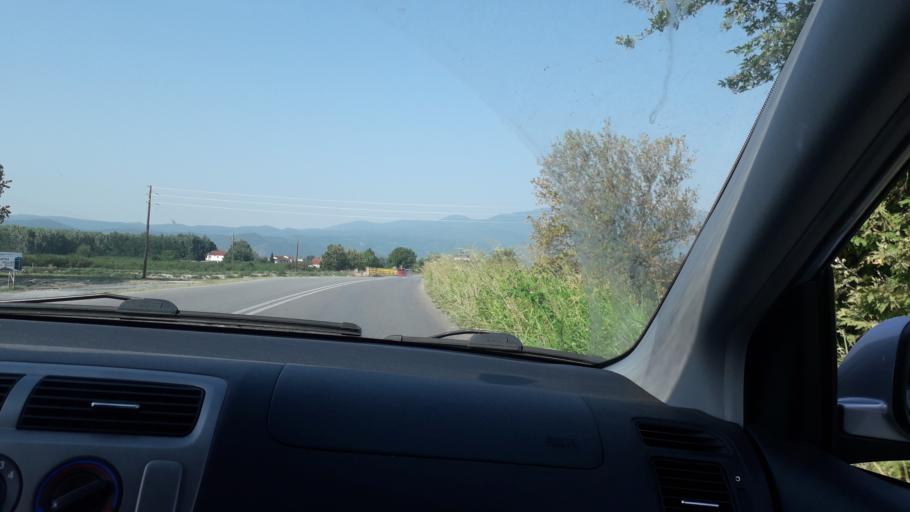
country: GR
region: Central Macedonia
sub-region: Nomos Pellis
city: Aridaia
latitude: 40.9617
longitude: 22.0494
